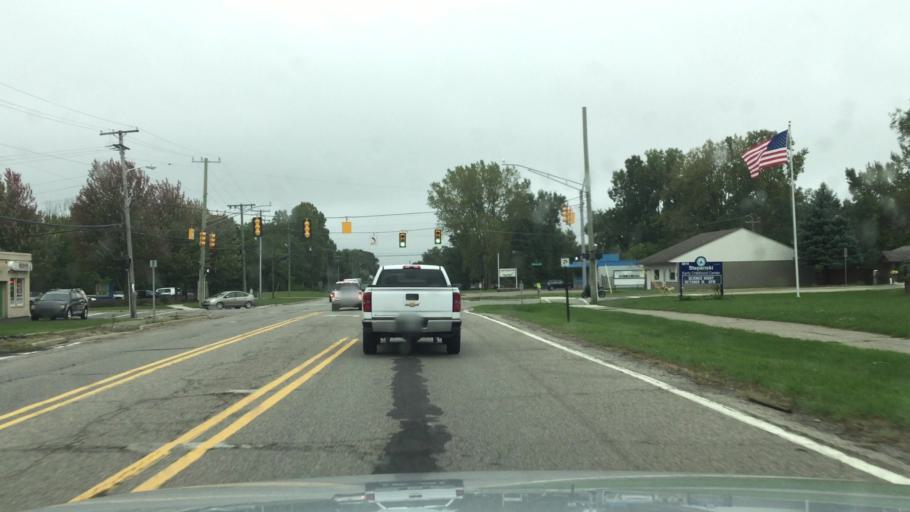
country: US
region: Michigan
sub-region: Oakland County
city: Waterford
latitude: 42.6751
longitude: -83.4067
